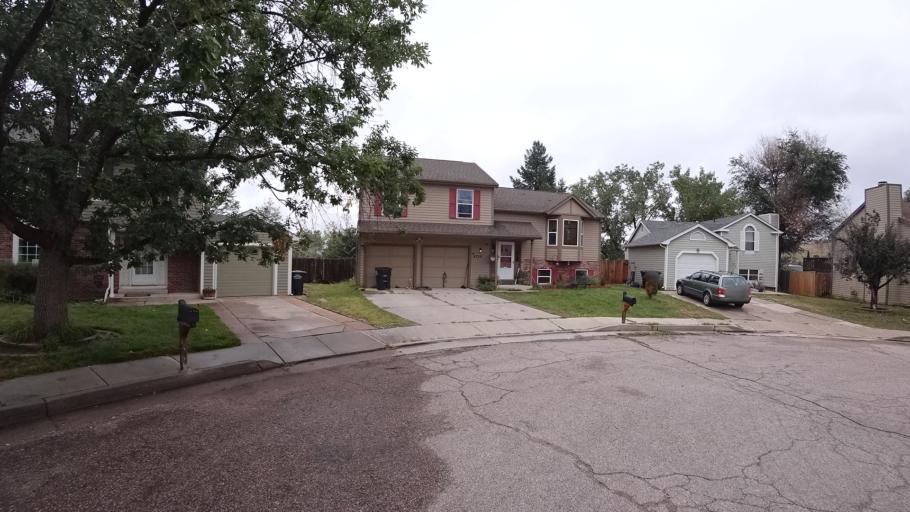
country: US
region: Colorado
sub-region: El Paso County
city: Cimarron Hills
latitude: 38.9290
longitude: -104.7657
